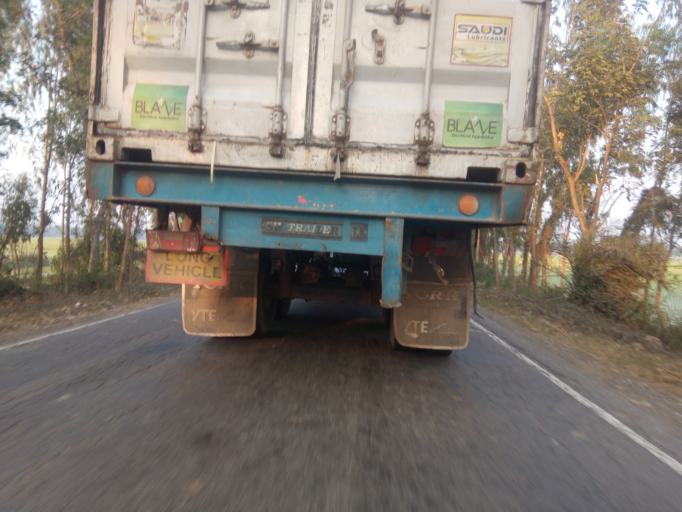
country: BD
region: Rajshahi
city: Bogra
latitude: 24.5662
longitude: 89.2093
